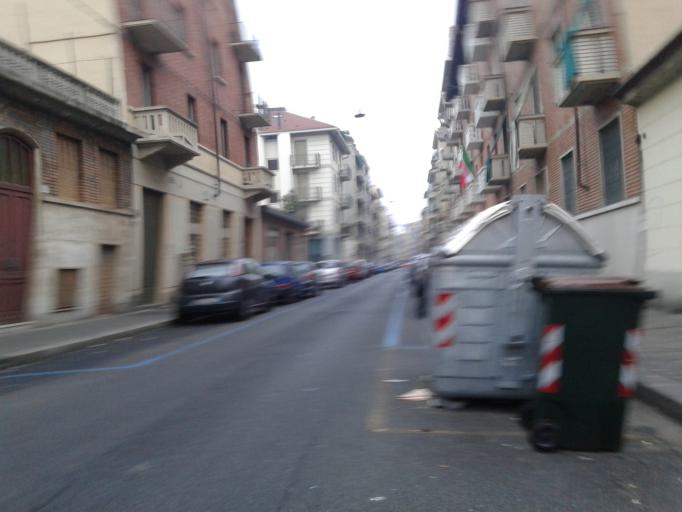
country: IT
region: Piedmont
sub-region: Provincia di Torino
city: Turin
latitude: 45.0830
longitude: 7.6624
